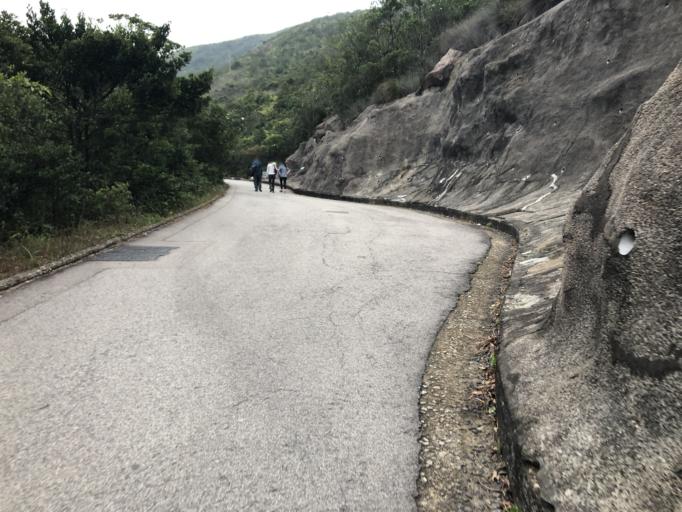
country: HK
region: Wanchai
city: Wan Chai
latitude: 22.2731
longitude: 114.2107
